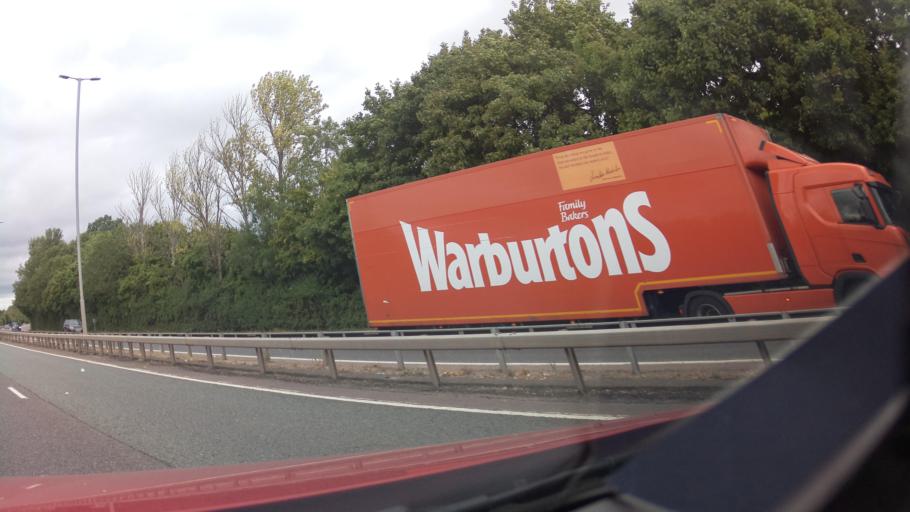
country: GB
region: England
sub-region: Nottinghamshire
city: Eastwood
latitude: 53.0056
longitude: -1.3060
